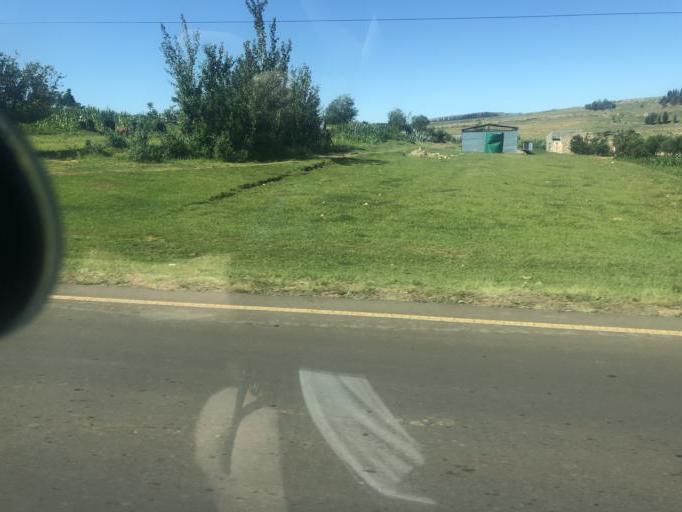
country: LS
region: Maseru
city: Maseru
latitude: -29.3643
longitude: 27.6264
